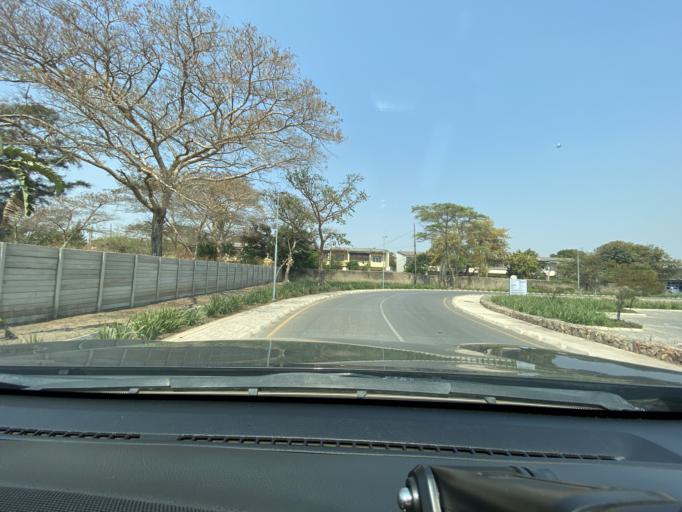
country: ZM
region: Lusaka
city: Lusaka
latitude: -15.3916
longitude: 28.3236
